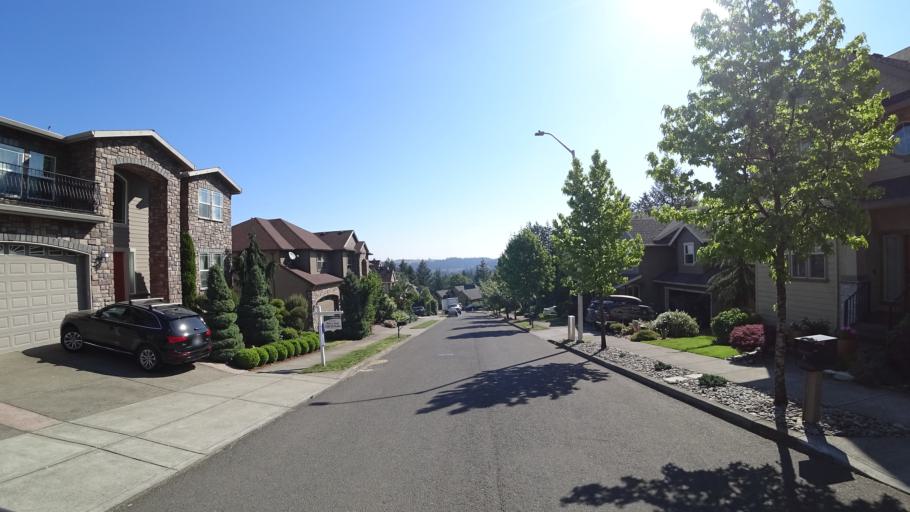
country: US
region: Oregon
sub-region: Clackamas County
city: Happy Valley
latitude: 45.4671
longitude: -122.5382
